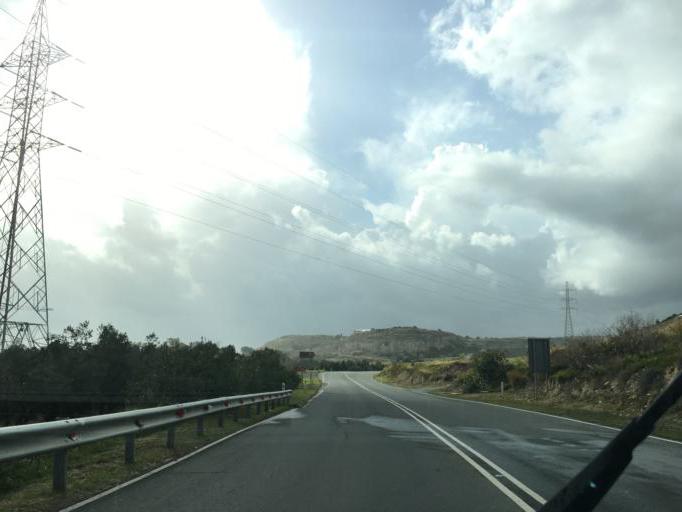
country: CY
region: Limassol
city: Erimi
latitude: 34.6638
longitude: 32.8989
